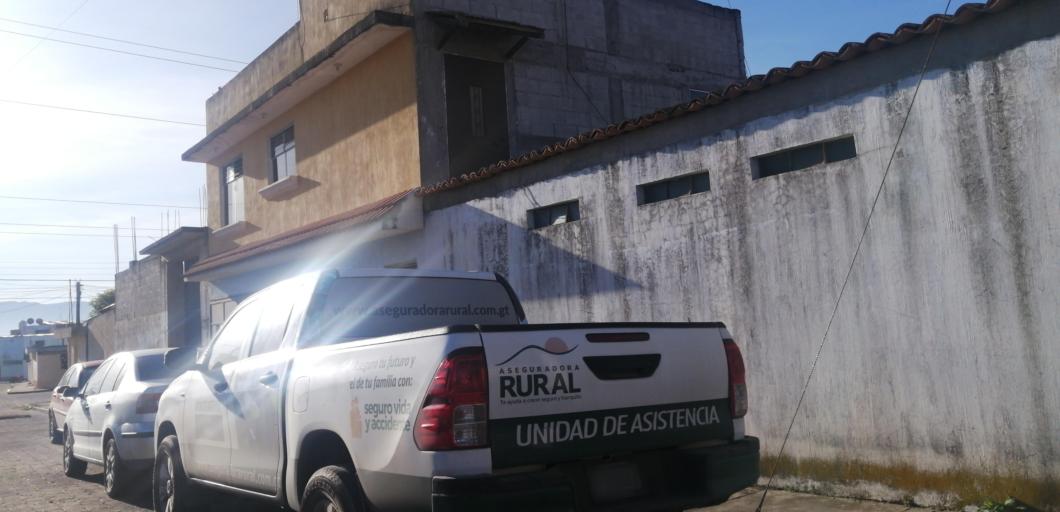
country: GT
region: Quetzaltenango
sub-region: Municipio de La Esperanza
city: La Esperanza
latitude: 14.8670
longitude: -91.5452
